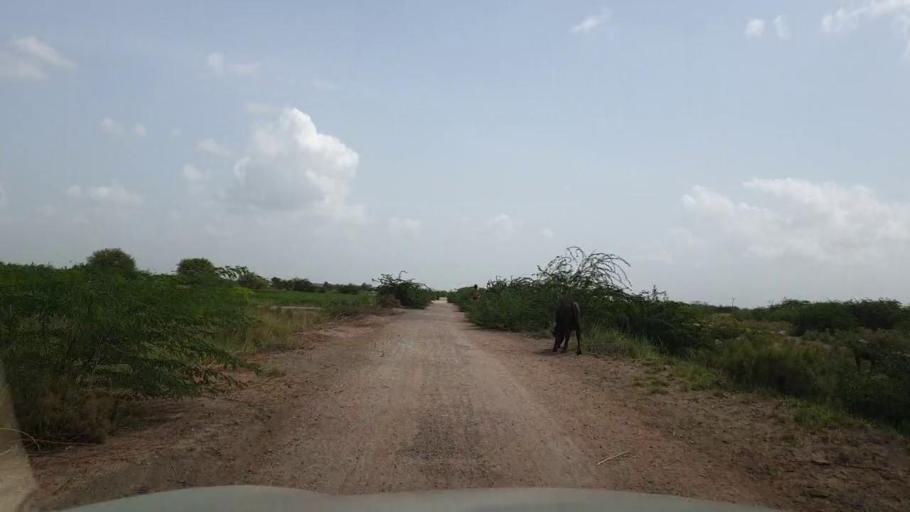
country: PK
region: Sindh
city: Kadhan
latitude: 24.3968
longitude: 68.7966
